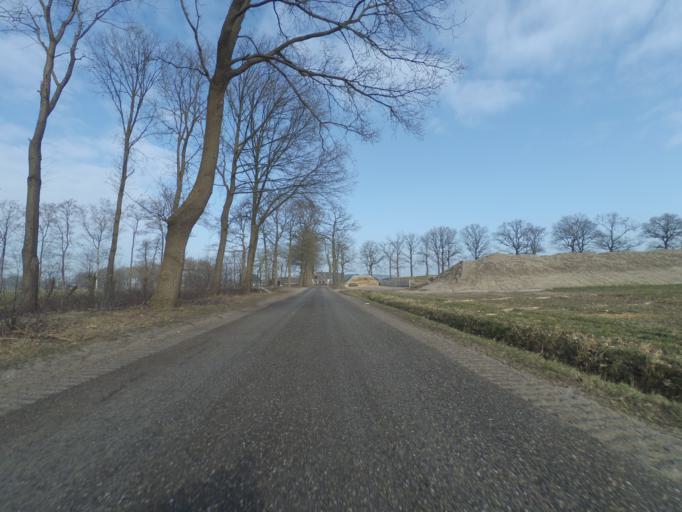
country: NL
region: Utrecht
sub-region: Gemeente Utrechtse Heuvelrug
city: Overberg
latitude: 52.0469
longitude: 5.4591
